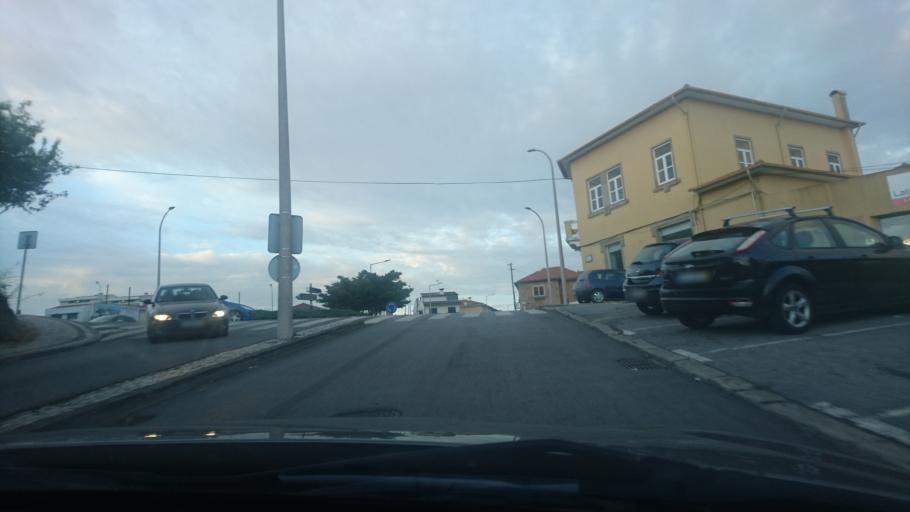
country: PT
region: Aveiro
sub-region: Sao Joao da Madeira
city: Sao Joao da Madeira
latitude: 40.8933
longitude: -8.4891
